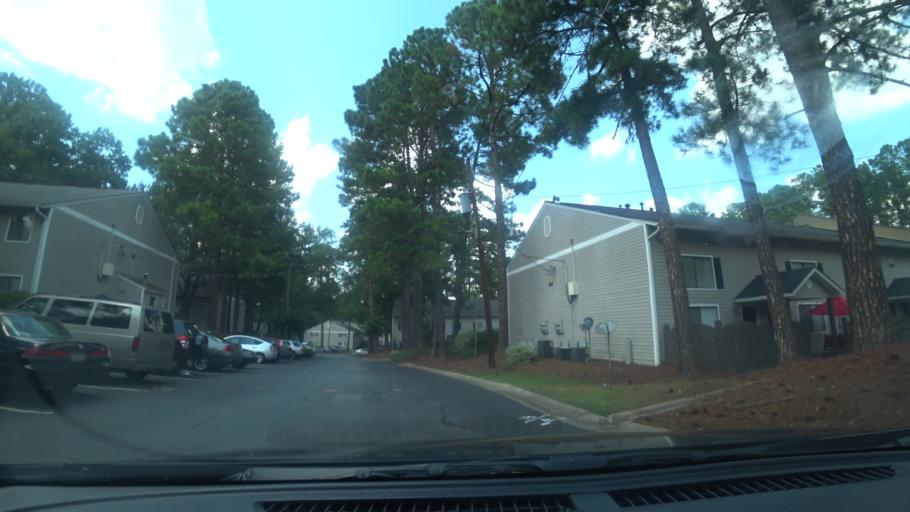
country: US
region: Georgia
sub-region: DeKalb County
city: Clarkston
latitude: 33.8214
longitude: -84.2278
